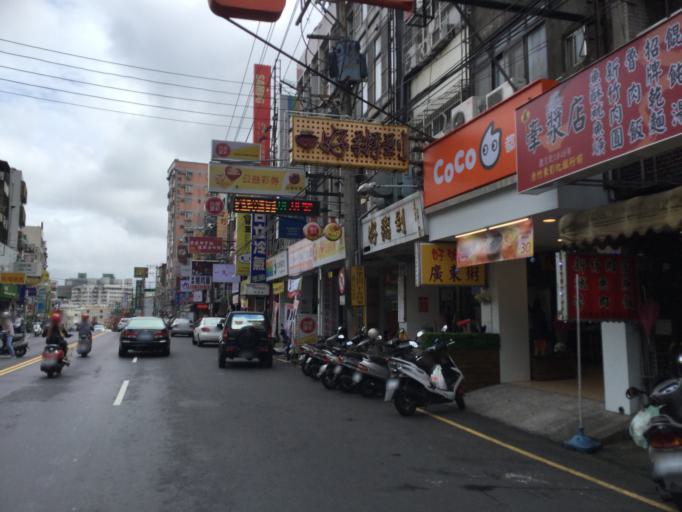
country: TW
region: Taiwan
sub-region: Hsinchu
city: Hsinchu
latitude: 24.7815
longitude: 121.0231
